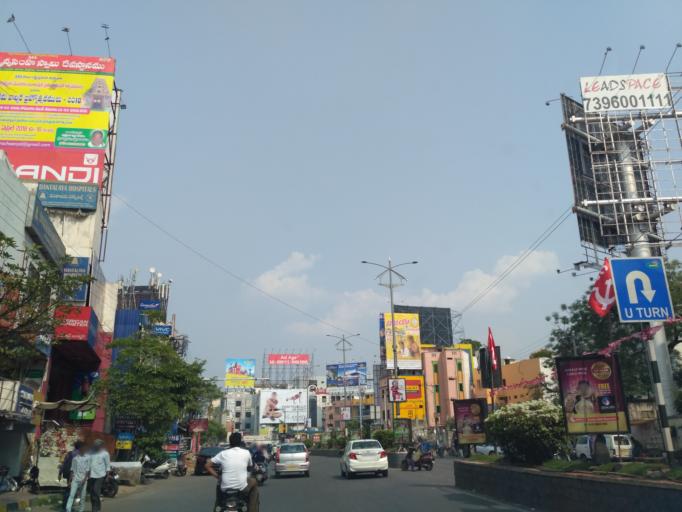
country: IN
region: Telangana
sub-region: Hyderabad
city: Hyderabad
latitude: 17.4010
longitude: 78.4868
